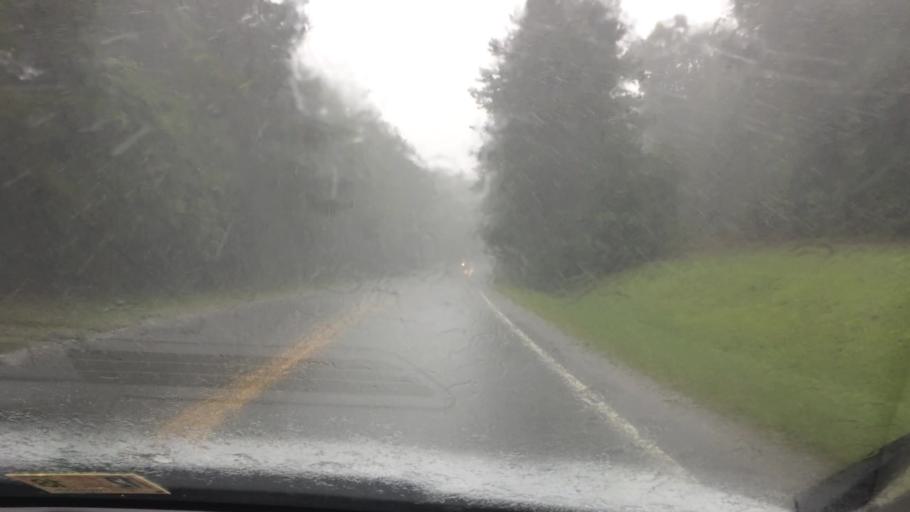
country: US
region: Virginia
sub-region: James City County
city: Williamsburg
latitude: 37.3868
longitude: -76.7660
